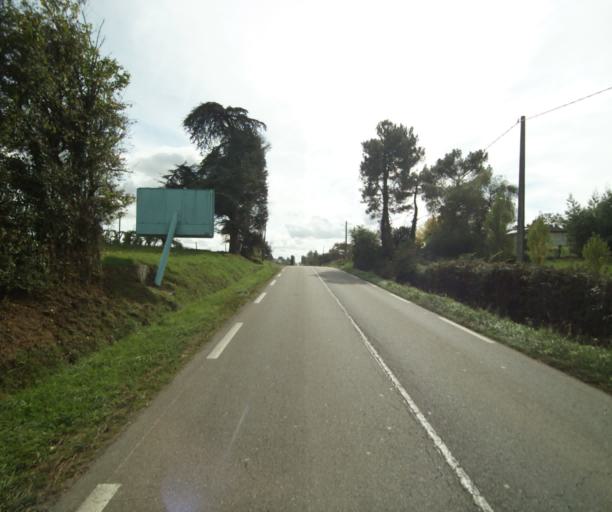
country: FR
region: Midi-Pyrenees
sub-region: Departement du Gers
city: Eauze
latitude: 43.8473
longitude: 0.0932
